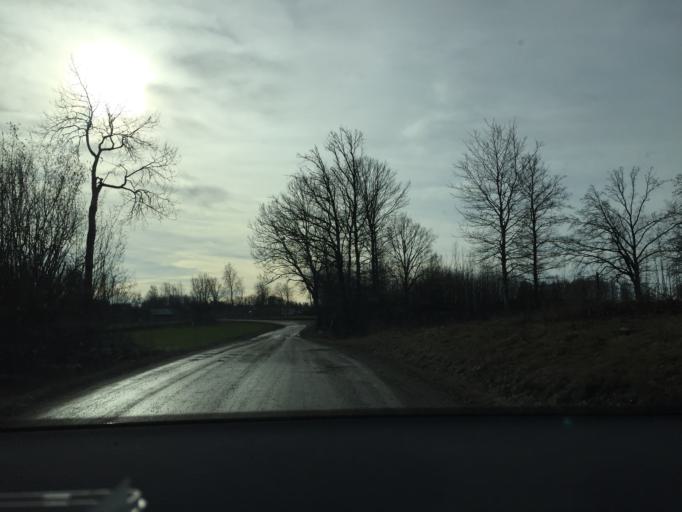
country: SE
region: OErebro
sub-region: Orebro Kommun
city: Odensbacken
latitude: 59.1371
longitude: 15.4745
